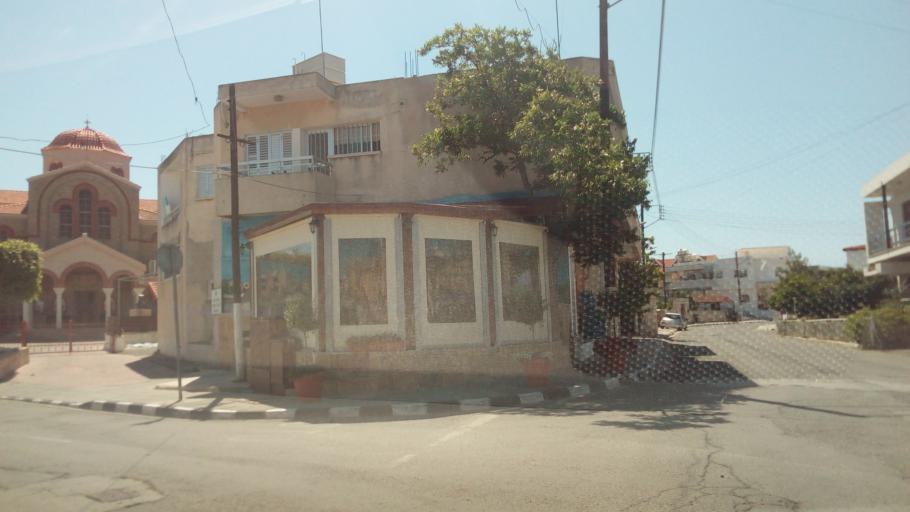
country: CY
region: Limassol
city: Parekklisha
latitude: 34.7436
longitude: 33.1600
